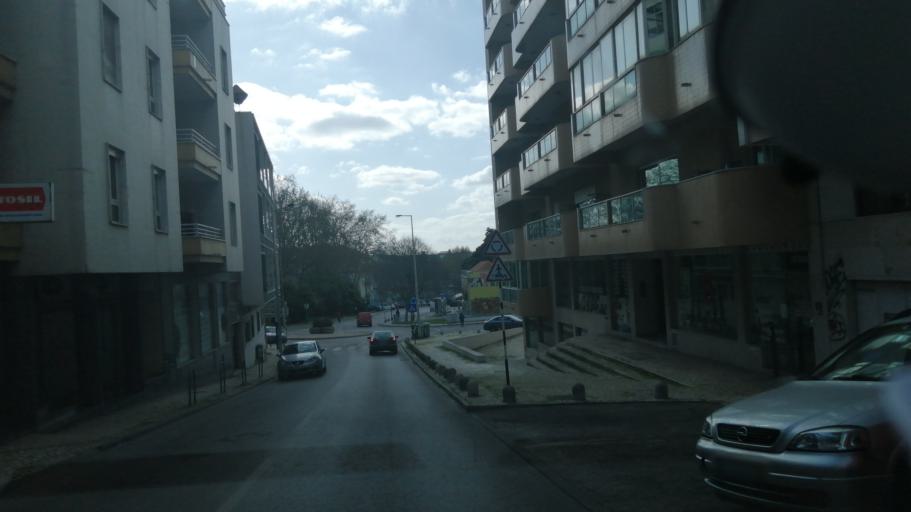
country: PT
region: Setubal
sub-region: Almada
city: Almada
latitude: 38.6752
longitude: -9.1625
